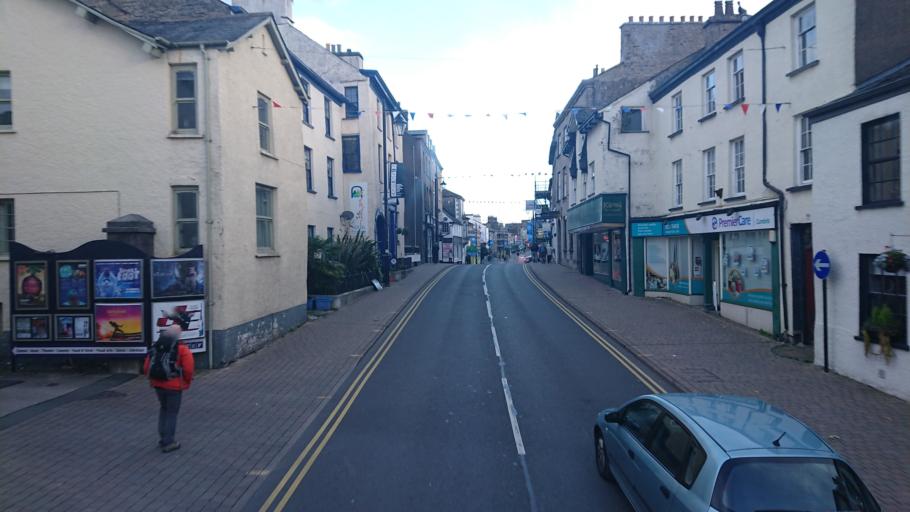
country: GB
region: England
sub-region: Cumbria
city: Kendal
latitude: 54.3244
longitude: -2.7474
